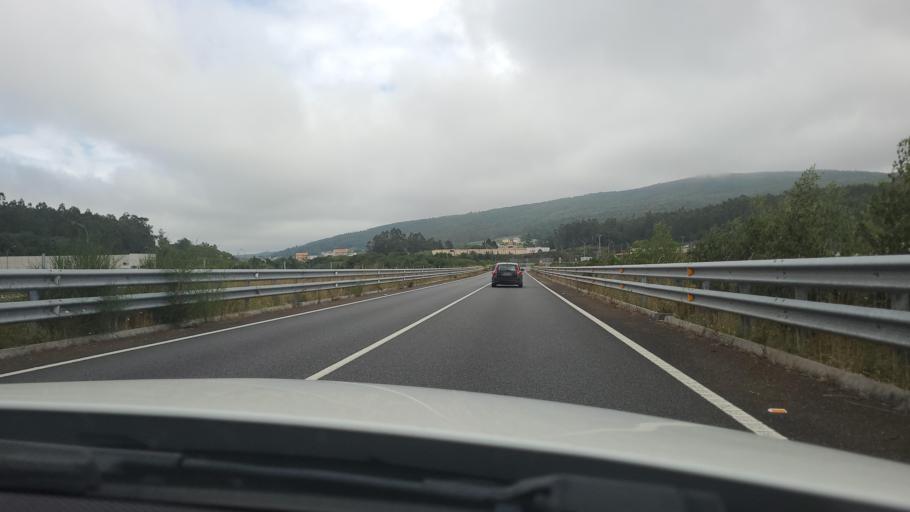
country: ES
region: Galicia
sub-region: Provincia da Coruna
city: Cee
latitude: 42.9751
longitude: -9.1936
